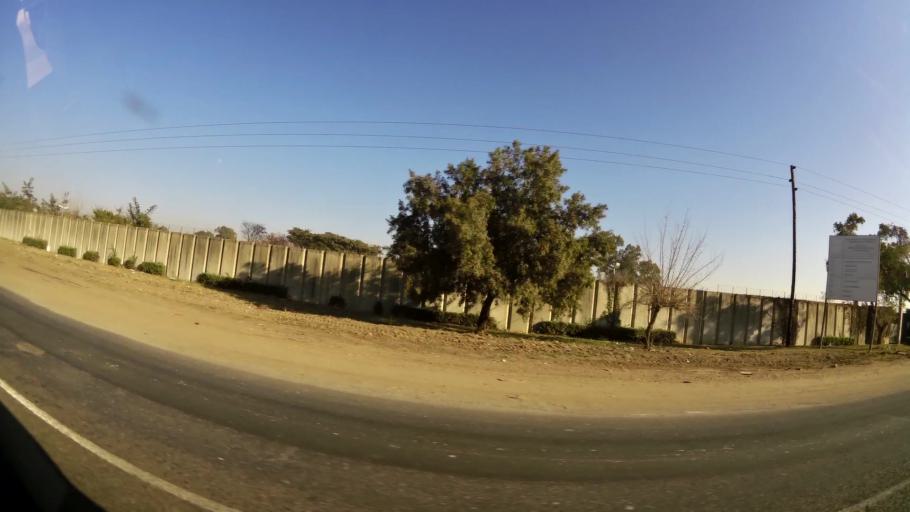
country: ZA
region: Gauteng
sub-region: City of Tshwane Metropolitan Municipality
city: Pretoria
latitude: -25.6498
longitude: 28.1929
